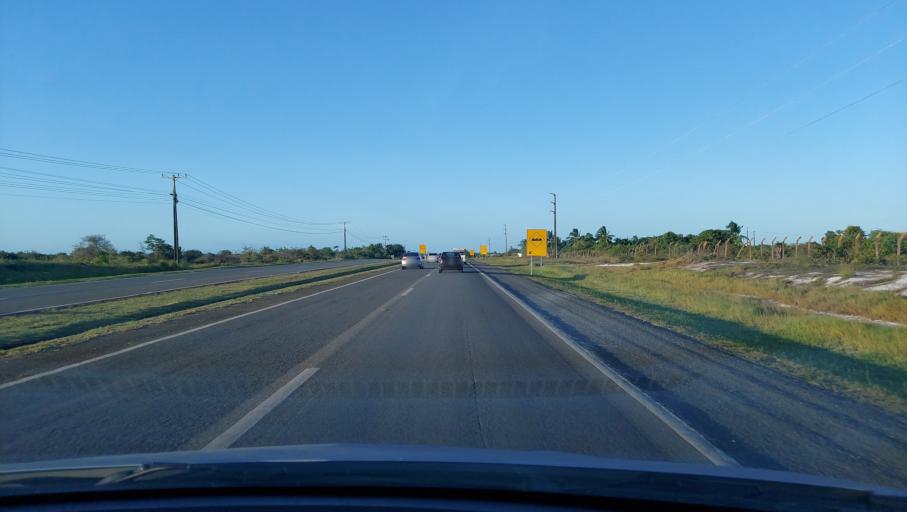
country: BR
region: Bahia
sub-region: Camacari
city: Camacari
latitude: -12.7432
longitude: -38.1656
